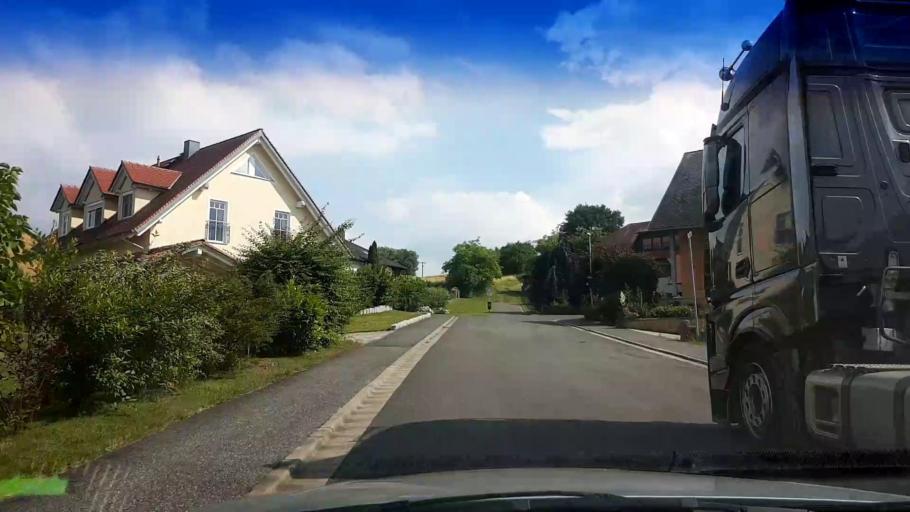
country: DE
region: Bavaria
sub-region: Upper Franconia
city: Viereth-Trunstadt
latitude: 49.9250
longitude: 10.7573
